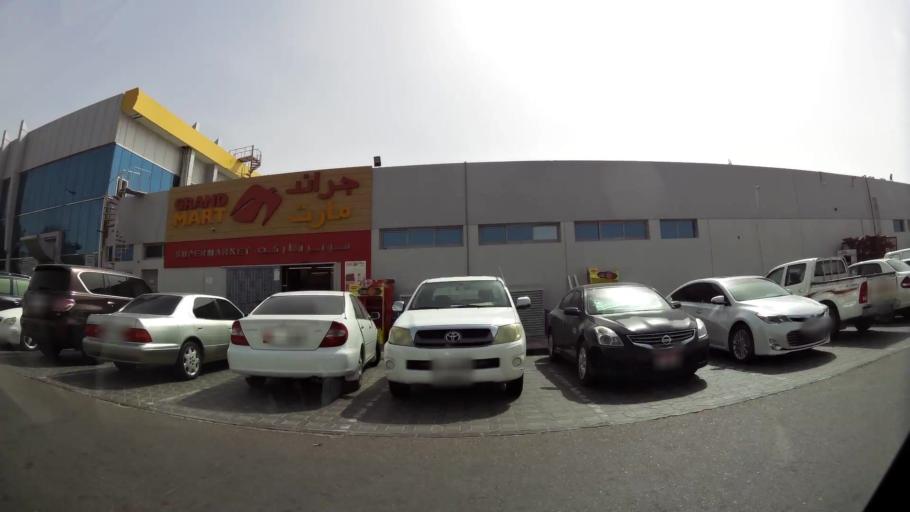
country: AE
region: Abu Dhabi
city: Al Ain
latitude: 24.1843
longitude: 55.6294
